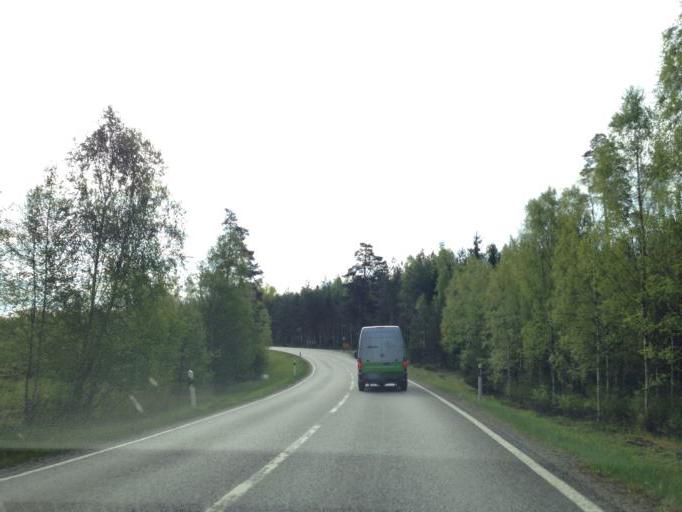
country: SE
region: Soedermanland
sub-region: Nykopings Kommun
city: Stigtomta
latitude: 58.8856
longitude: 16.8439
